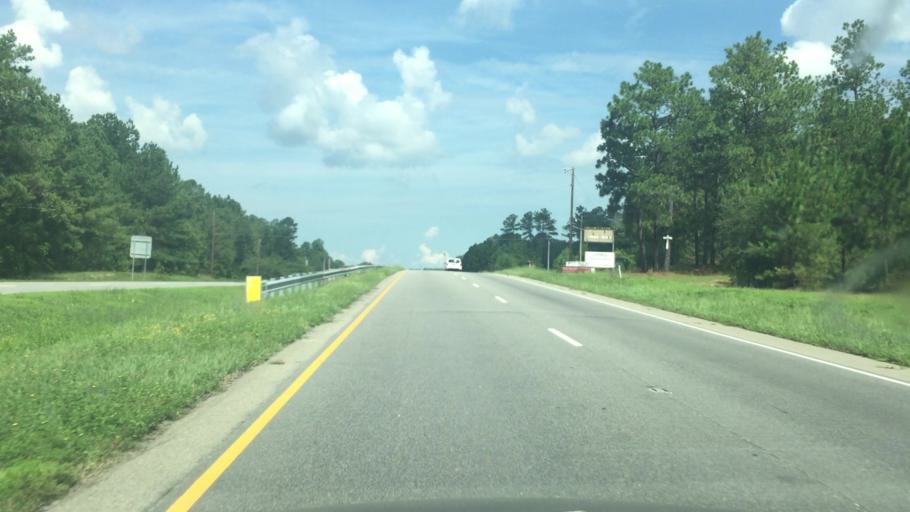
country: US
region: North Carolina
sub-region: Richmond County
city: Hamlet
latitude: 34.8622
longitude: -79.6342
